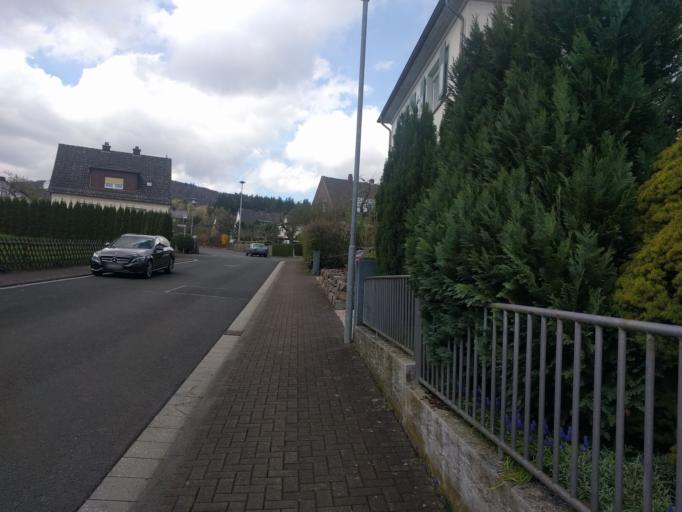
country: DE
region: Hesse
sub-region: Regierungsbezirk Giessen
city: Heuchelheim
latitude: 50.6430
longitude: 8.5979
